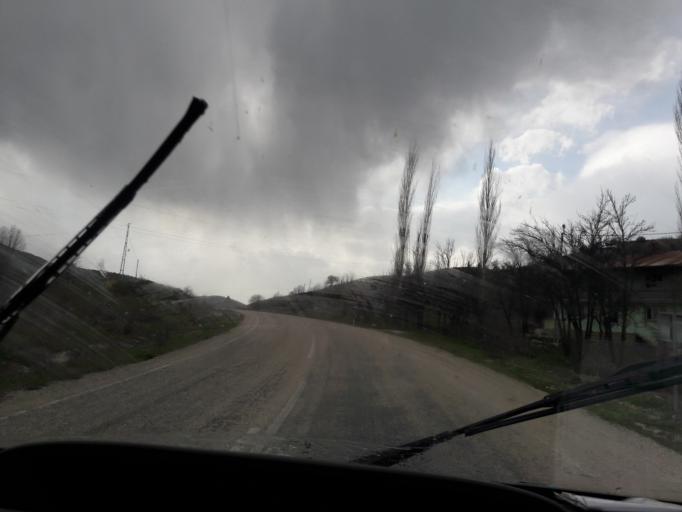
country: TR
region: Giresun
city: Alucra
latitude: 40.2979
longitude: 38.8021
